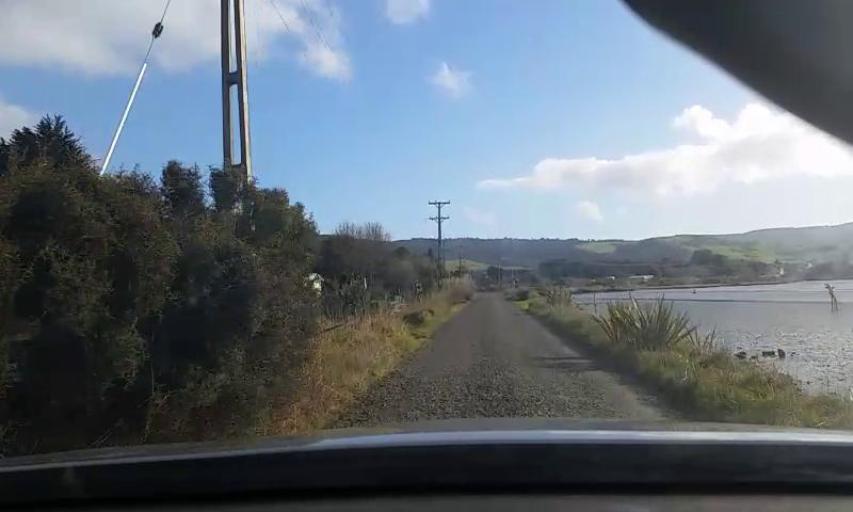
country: NZ
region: Otago
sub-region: Clutha District
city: Papatowai
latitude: -46.6290
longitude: 169.1385
